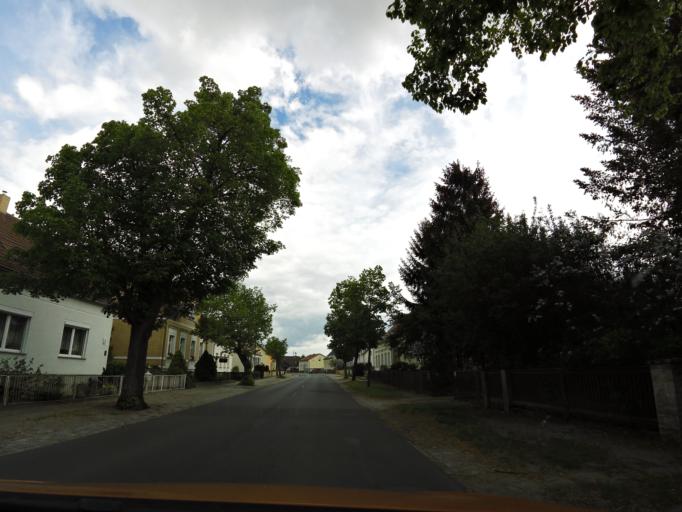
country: DE
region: Brandenburg
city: Michendorf
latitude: 52.3195
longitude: 13.1237
